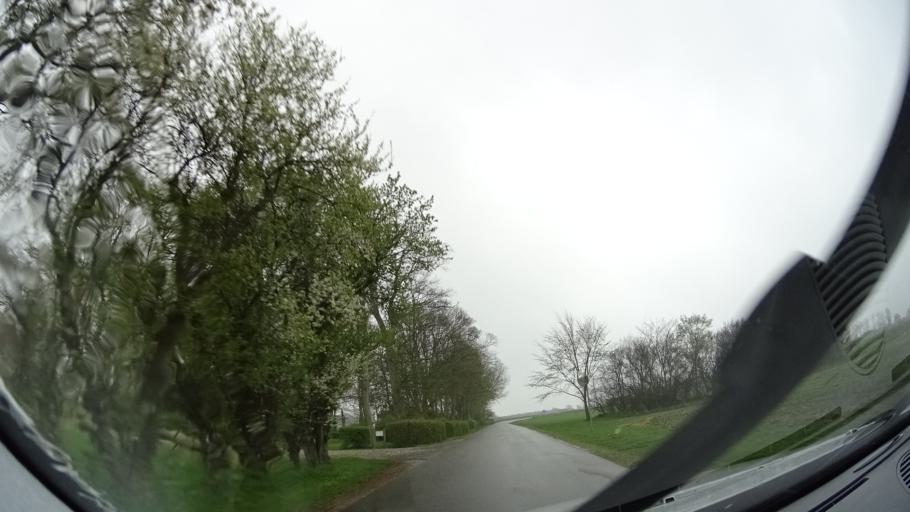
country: DK
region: Zealand
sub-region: Holbaek Kommune
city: Holbaek
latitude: 55.7149
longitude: 11.7740
